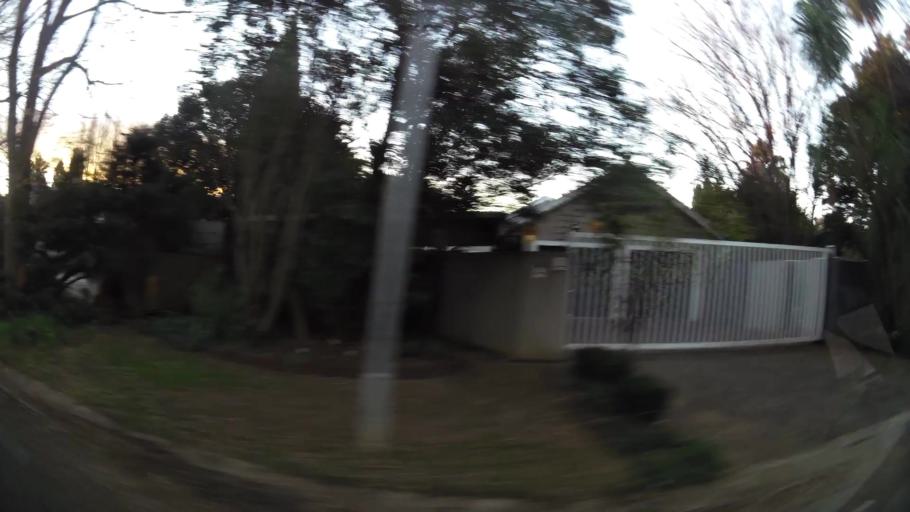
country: ZA
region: North-West
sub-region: Dr Kenneth Kaunda District Municipality
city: Potchefstroom
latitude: -26.7237
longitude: 27.1108
